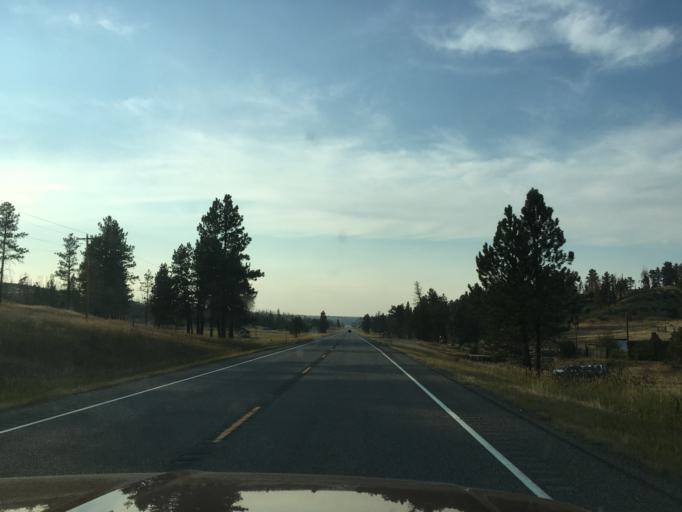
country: US
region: Montana
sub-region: Musselshell County
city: Roundup
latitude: 46.2787
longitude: -108.4754
